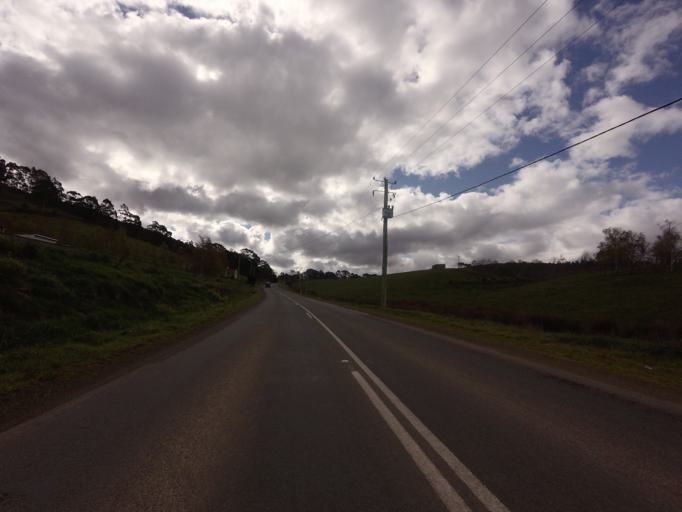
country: AU
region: Tasmania
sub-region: Huon Valley
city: Geeveston
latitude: -43.1850
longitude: 146.9555
